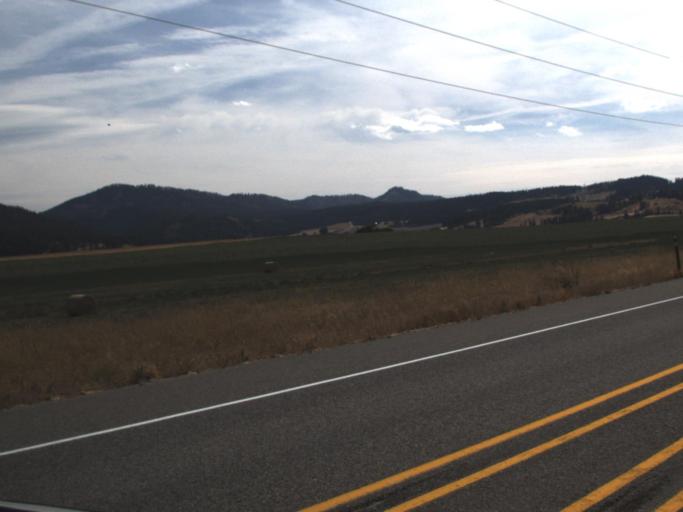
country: US
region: Washington
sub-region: Stevens County
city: Chewelah
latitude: 48.2353
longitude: -117.7153
